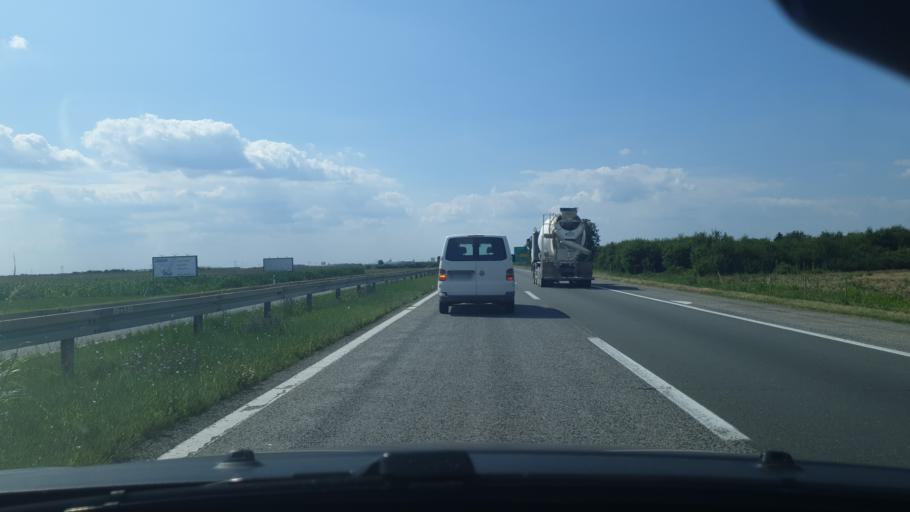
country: RS
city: Ugrinovci
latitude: 44.8650
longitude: 20.1488
